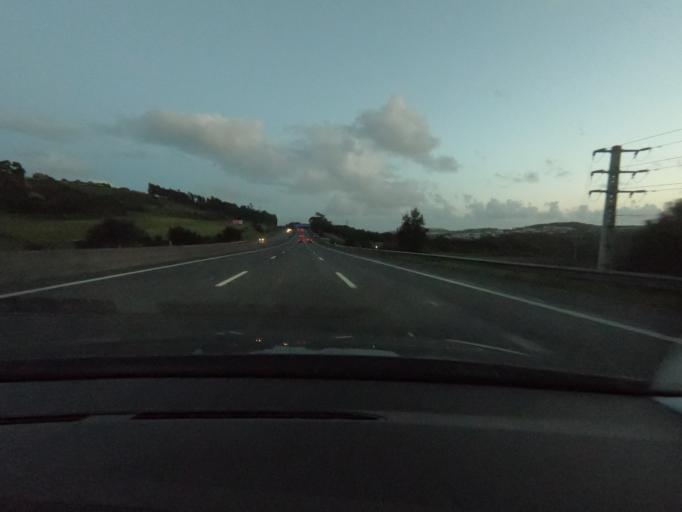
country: PT
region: Lisbon
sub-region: Oeiras
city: Barcarena
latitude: 38.7276
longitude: -9.2741
